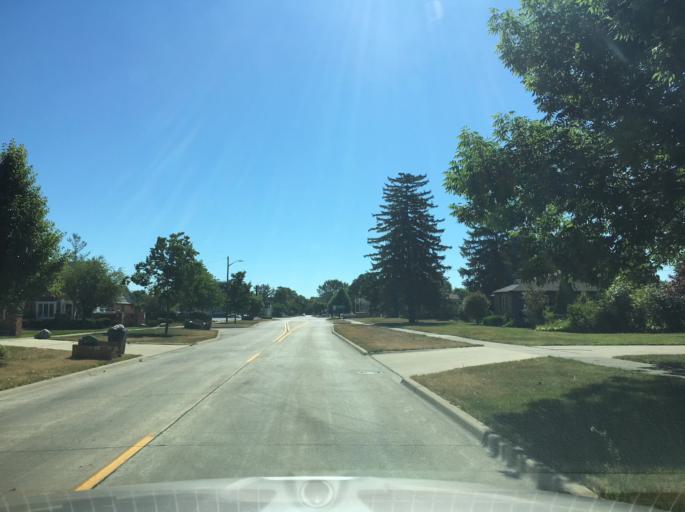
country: US
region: Michigan
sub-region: Macomb County
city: Saint Clair Shores
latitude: 42.5029
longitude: -82.9002
